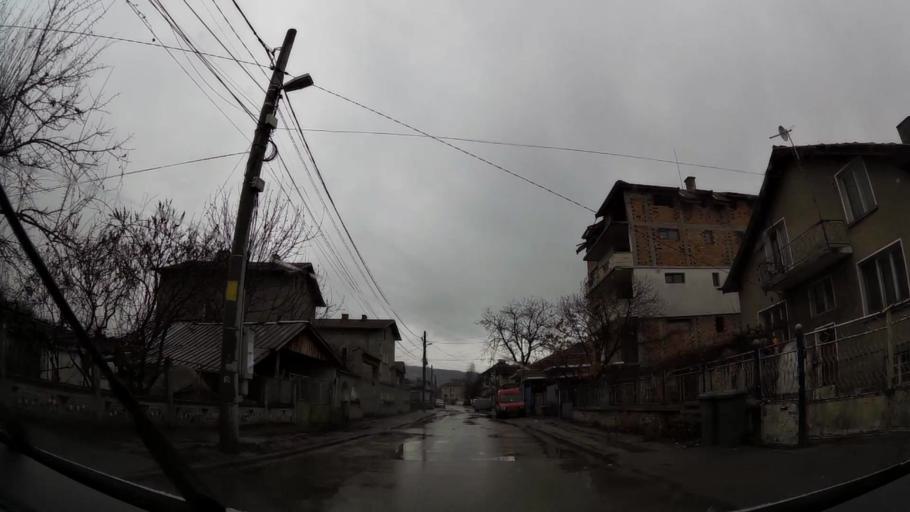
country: BG
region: Sofia-Capital
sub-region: Stolichna Obshtina
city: Sofia
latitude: 42.6293
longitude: 23.4124
